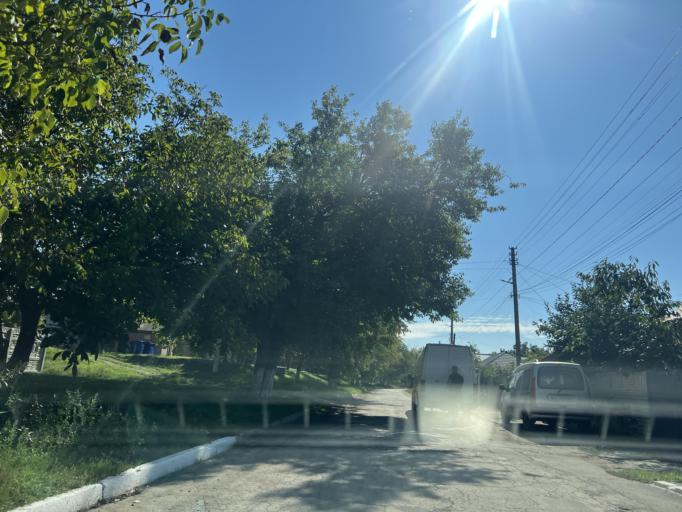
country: RO
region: Iasi
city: Ungheni-Prut
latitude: 47.1967
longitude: 27.7966
